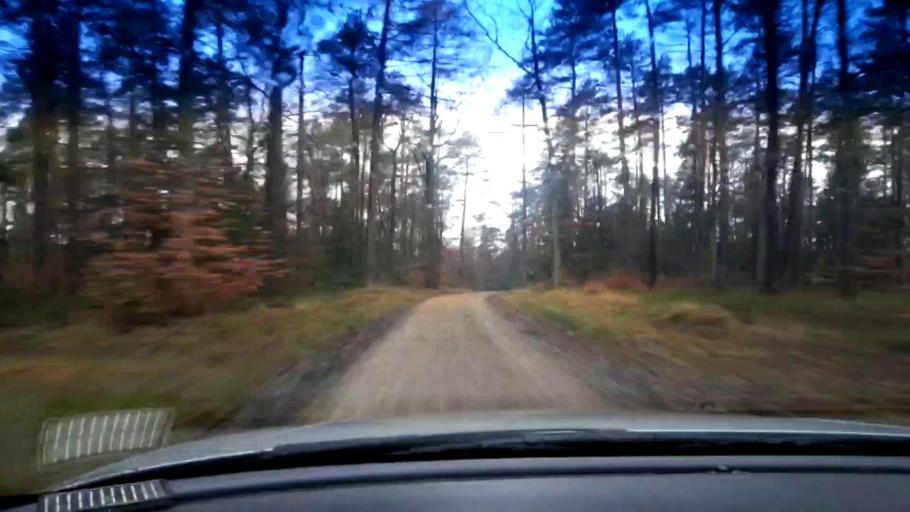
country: DE
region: Bavaria
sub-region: Upper Franconia
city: Gundelsheim
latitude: 49.9523
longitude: 10.9152
